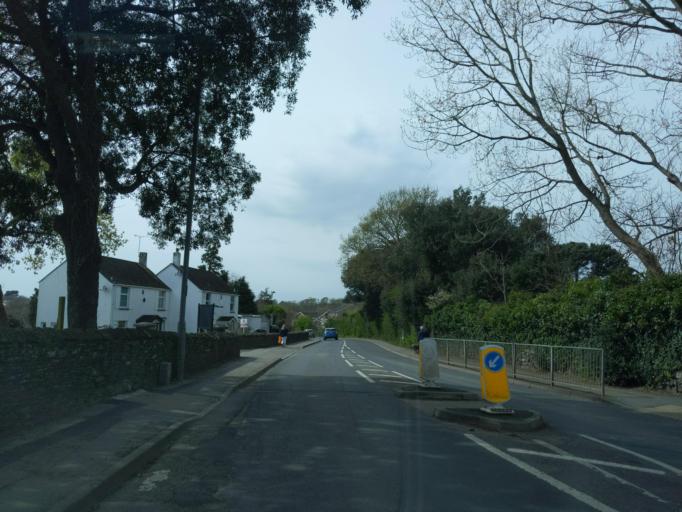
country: GB
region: England
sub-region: Cornwall
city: Torpoint
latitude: 50.3752
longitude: -4.2080
